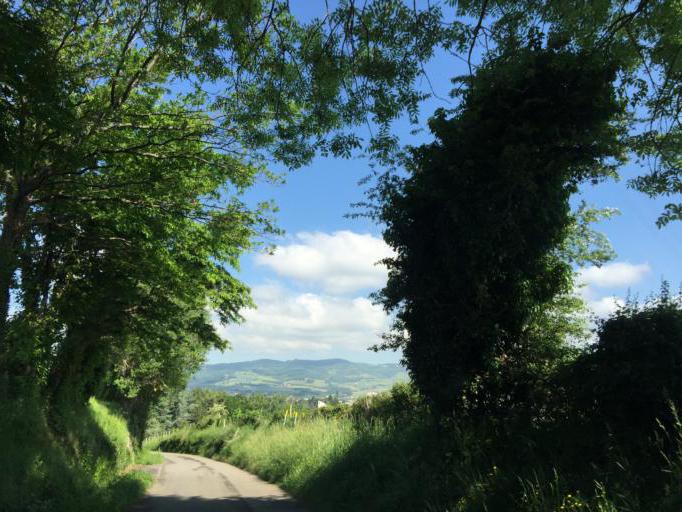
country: FR
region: Rhone-Alpes
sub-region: Departement de la Loire
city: Saint-Chamond
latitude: 45.4627
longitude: 4.5384
